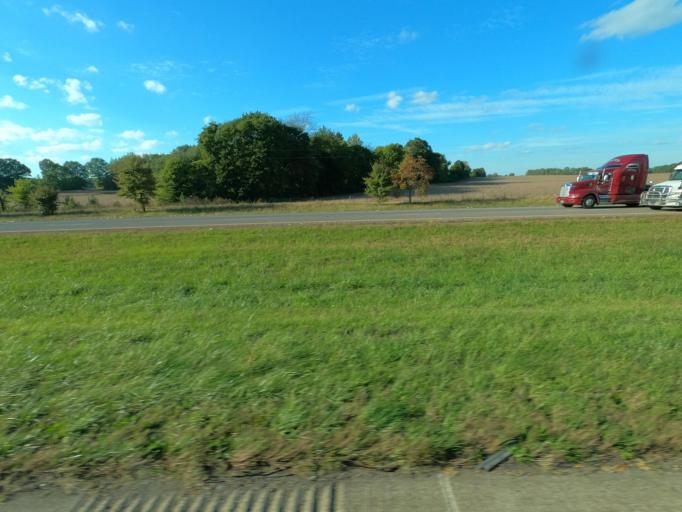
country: US
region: Tennessee
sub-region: Gibson County
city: Medina
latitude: 35.7038
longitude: -88.6770
